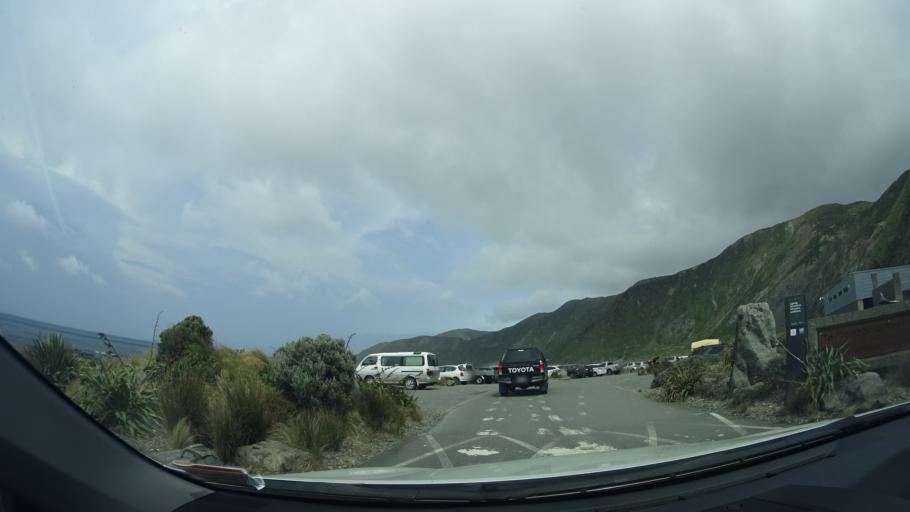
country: NZ
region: Wellington
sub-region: Wellington City
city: Brooklyn
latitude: -41.3487
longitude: 174.7504
